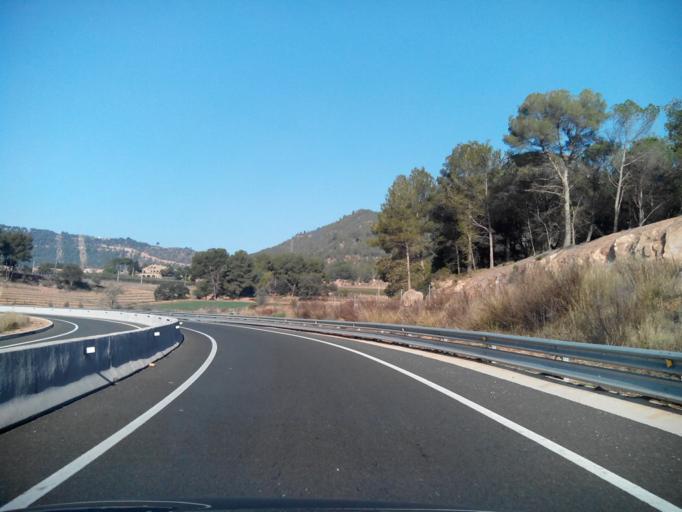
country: ES
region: Catalonia
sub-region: Provincia de Barcelona
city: Sant Joan de Vilatorrada
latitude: 41.7331
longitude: 1.7855
